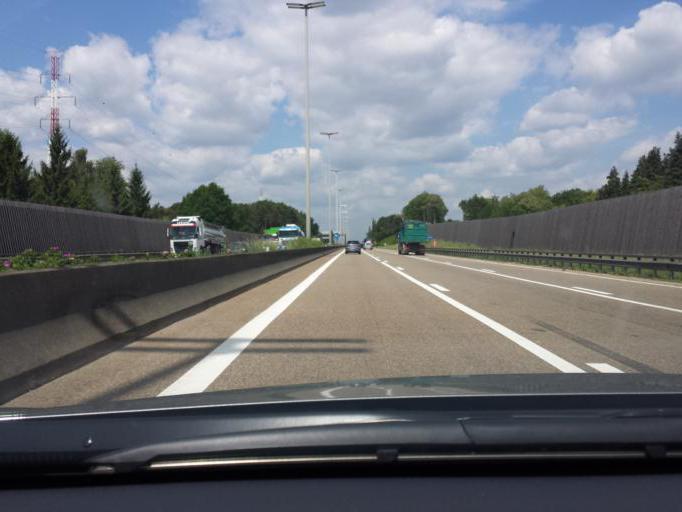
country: BE
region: Flanders
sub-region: Provincie Limburg
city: Lummen
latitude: 51.0070
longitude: 5.2179
